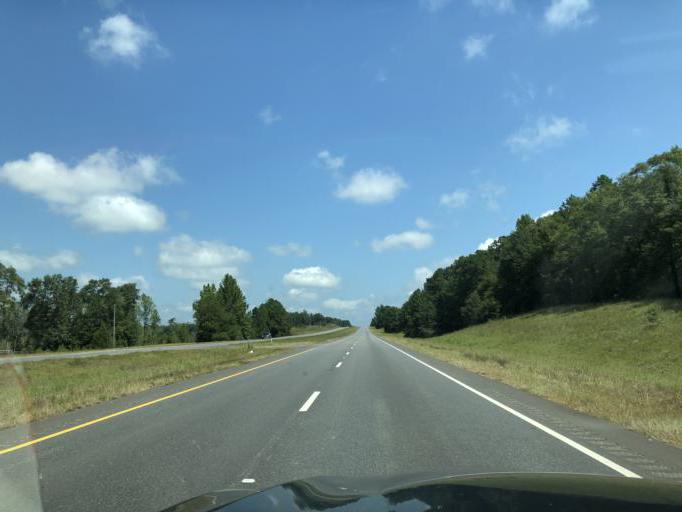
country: US
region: Alabama
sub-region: Henry County
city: Abbeville
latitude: 31.4713
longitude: -85.3036
